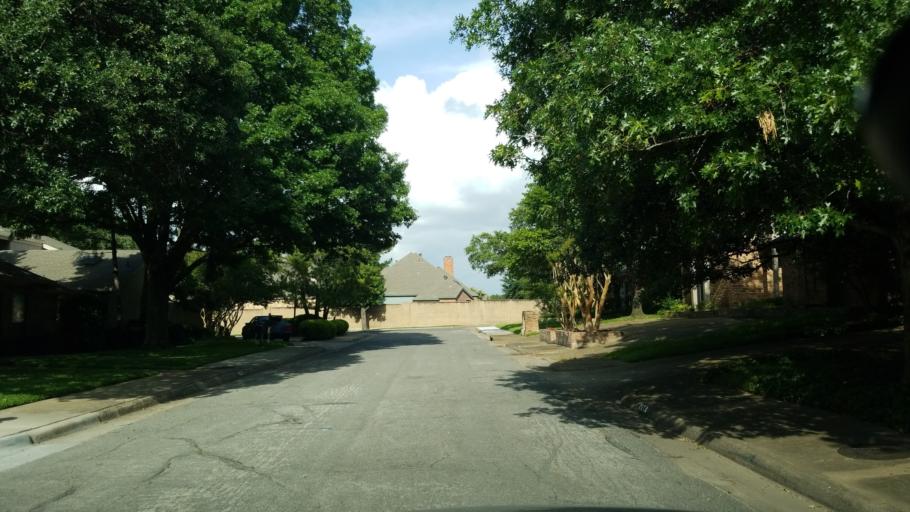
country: US
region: Texas
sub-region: Dallas County
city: University Park
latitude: 32.8701
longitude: -96.7839
